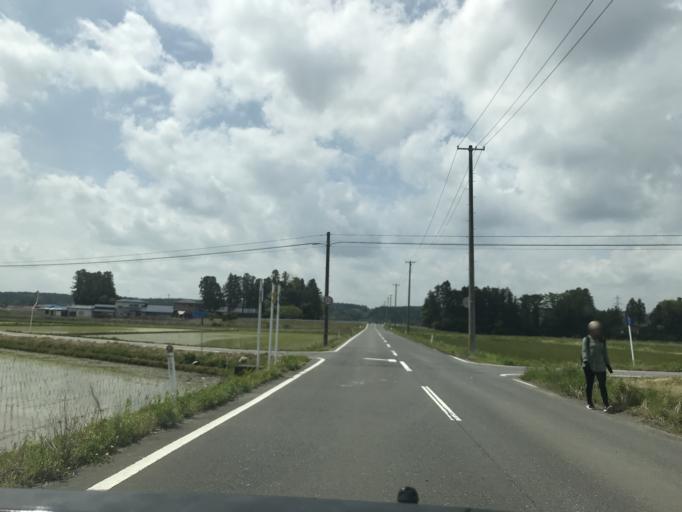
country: JP
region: Miyagi
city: Furukawa
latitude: 38.7515
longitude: 140.9363
